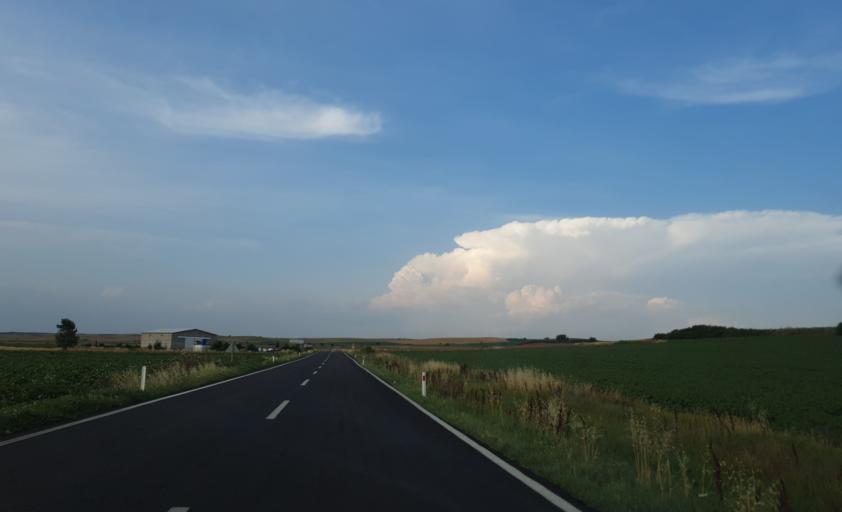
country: TR
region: Tekirdag
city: Hayrabolu
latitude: 41.2364
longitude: 27.1298
